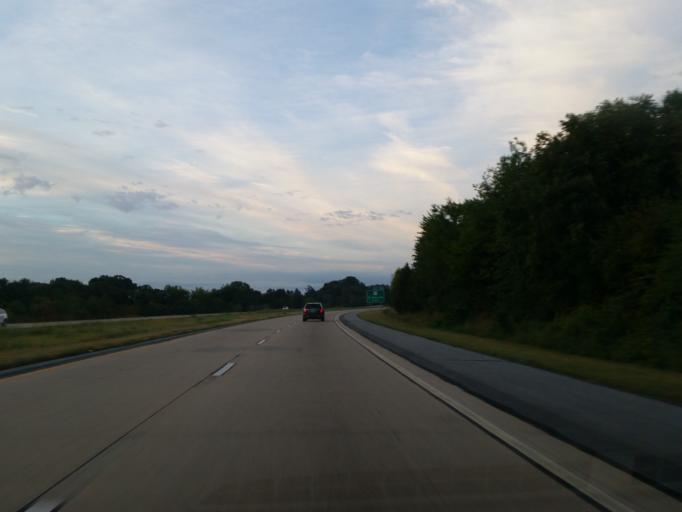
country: US
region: Delaware
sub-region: Kent County
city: Smyrna
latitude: 39.3036
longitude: -75.5937
